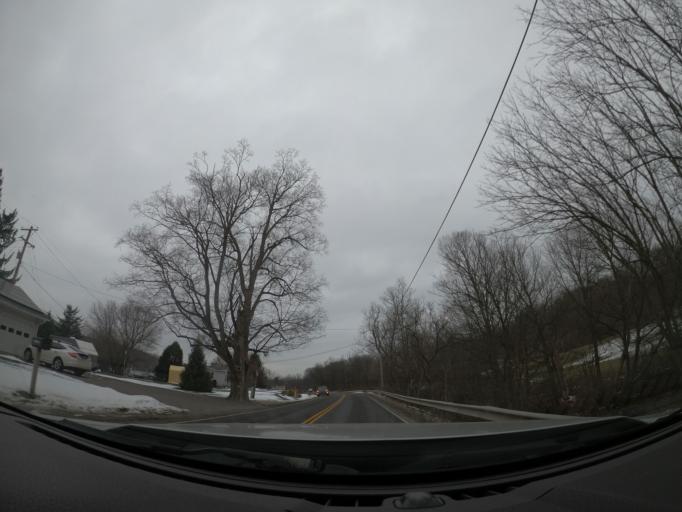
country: US
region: New York
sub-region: Cayuga County
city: Moravia
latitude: 42.6417
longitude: -76.4483
